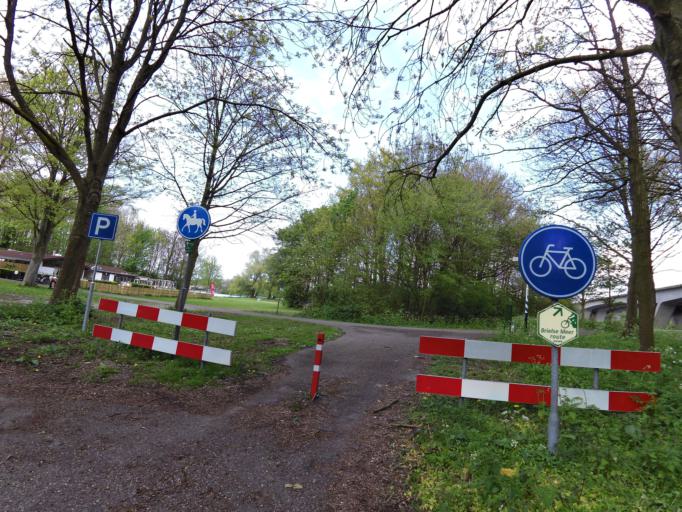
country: NL
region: South Holland
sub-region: Gemeente Brielle
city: Brielle
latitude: 51.8984
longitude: 4.2046
